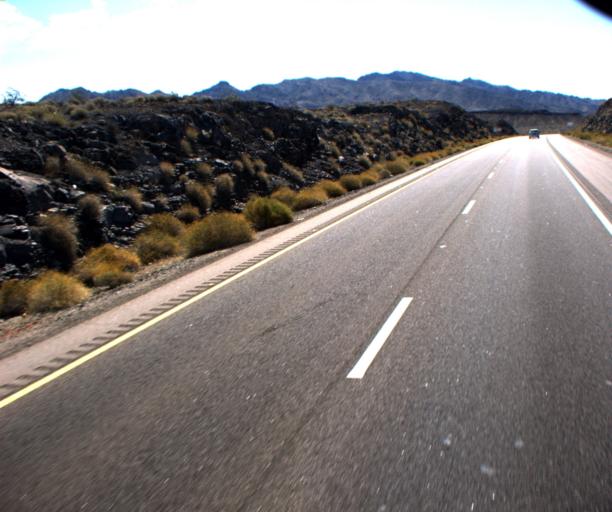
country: US
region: Nevada
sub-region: Clark County
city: Boulder City
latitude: 35.9514
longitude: -114.6502
